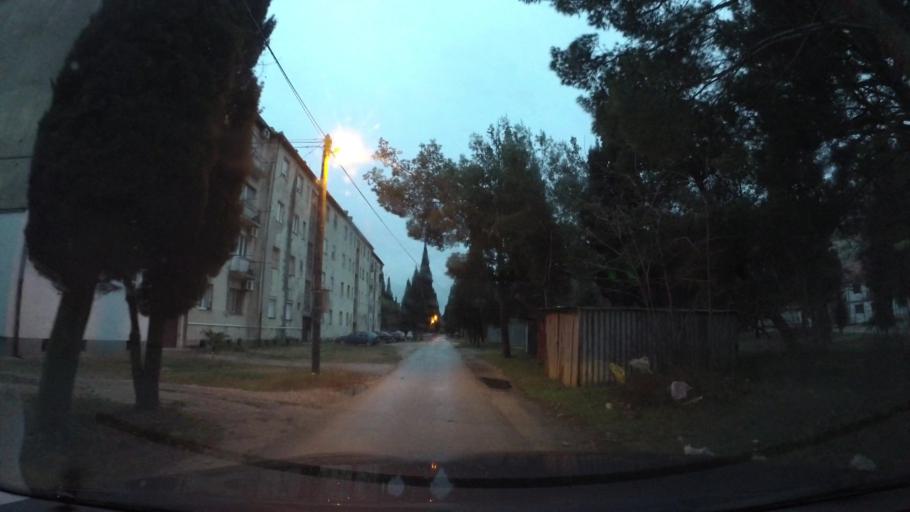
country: BA
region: Federation of Bosnia and Herzegovina
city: Rodoc
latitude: 43.3215
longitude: 17.8188
